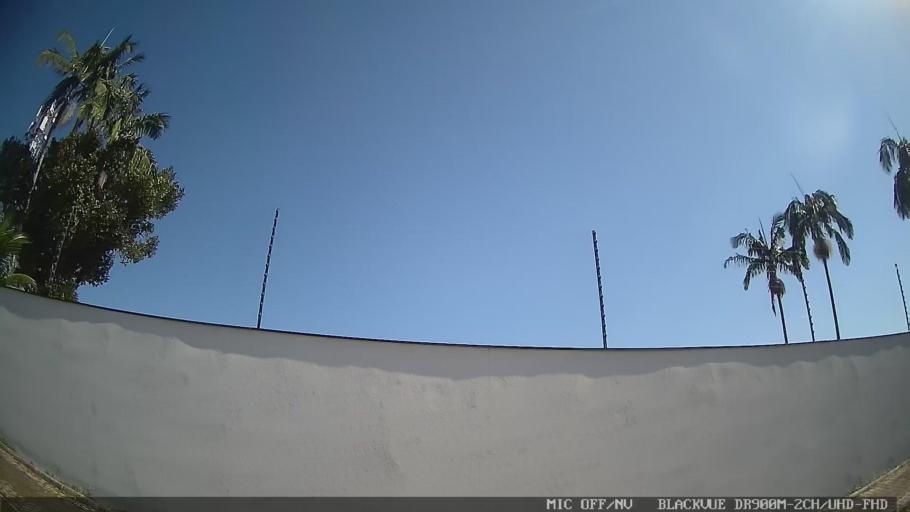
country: BR
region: Sao Paulo
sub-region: Guaruja
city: Guaruja
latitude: -23.9821
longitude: -46.2096
